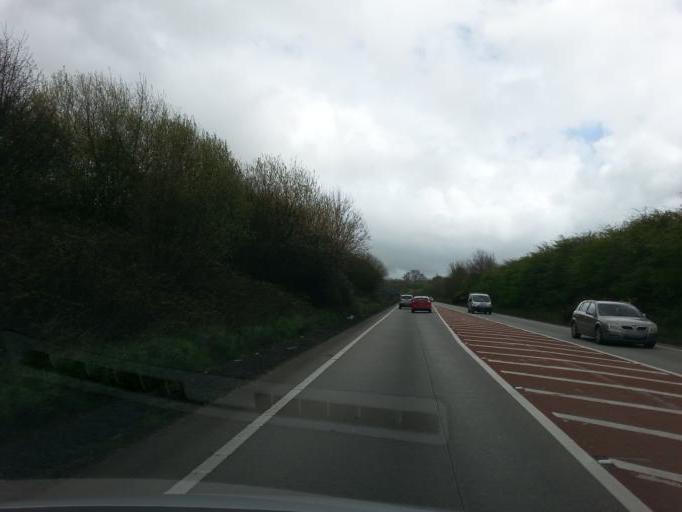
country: GB
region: England
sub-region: Somerset
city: Ilminster
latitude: 50.9364
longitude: -2.8738
